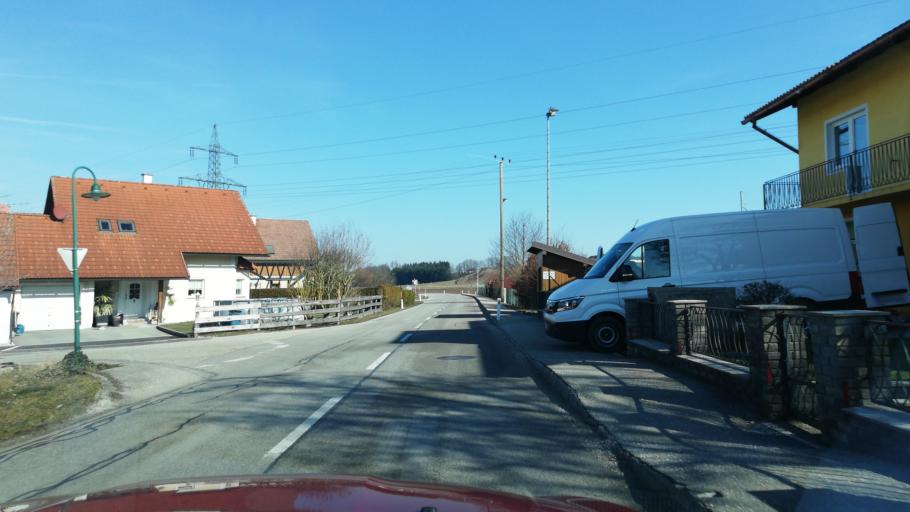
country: AT
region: Upper Austria
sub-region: Politischer Bezirk Vocklabruck
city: Rustorf
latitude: 48.0447
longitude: 13.7948
